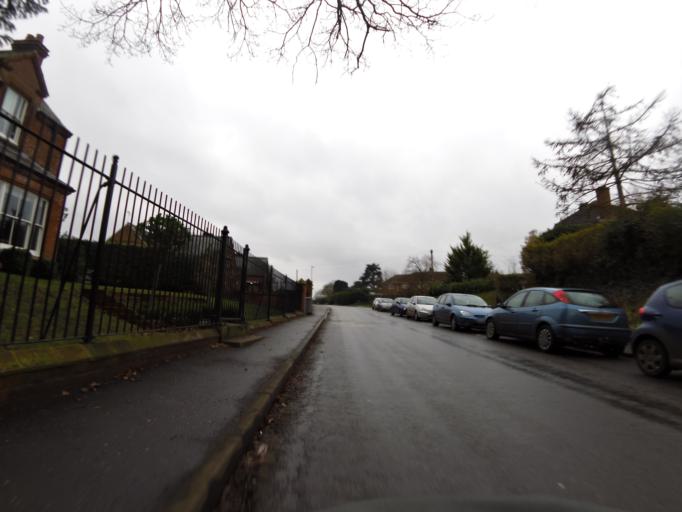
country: GB
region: England
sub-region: Norfolk
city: Briston
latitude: 52.7606
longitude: 1.1093
